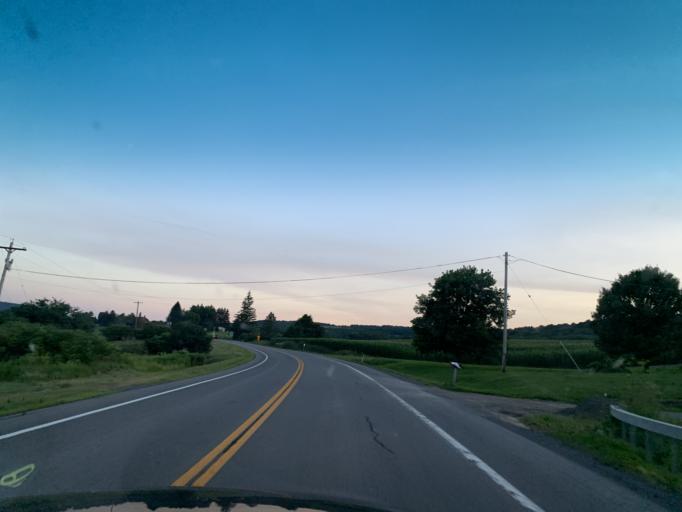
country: US
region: New York
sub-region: Chenango County
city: New Berlin
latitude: 42.7864
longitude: -75.2660
